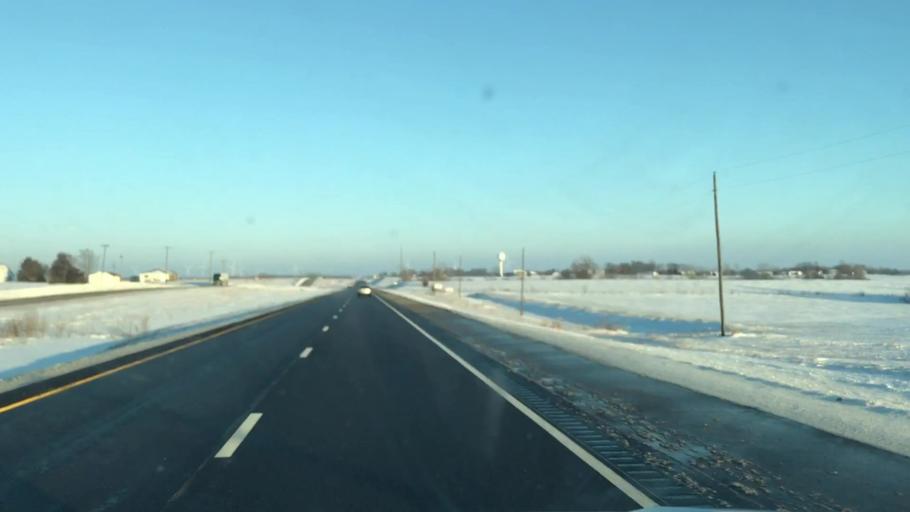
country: US
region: Missouri
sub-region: Clinton County
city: Gower
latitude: 39.7620
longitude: -94.5206
